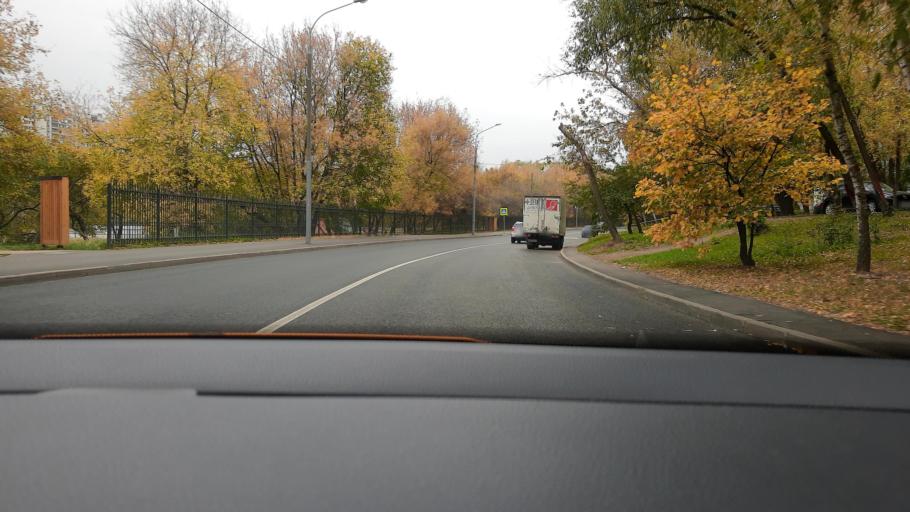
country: RU
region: Moscow
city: Leonovo
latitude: 55.8699
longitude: 37.6471
